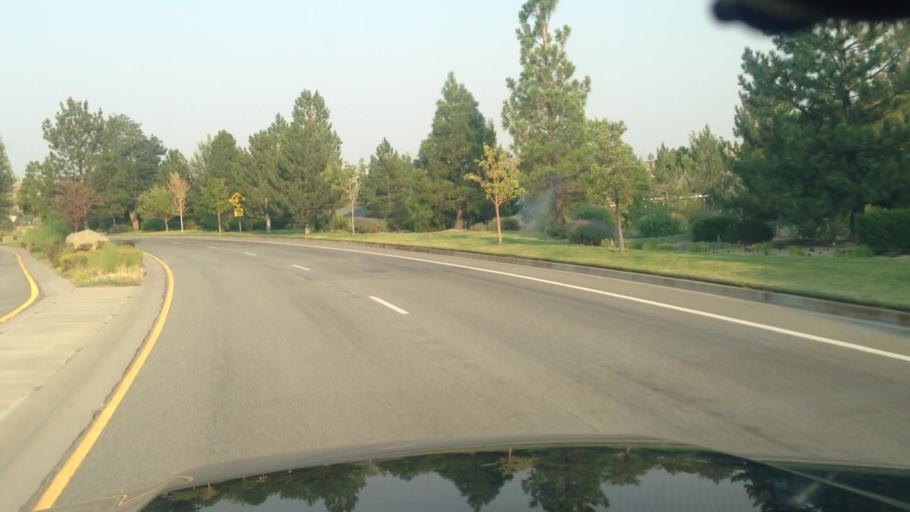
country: US
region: Nevada
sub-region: Washoe County
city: Mogul
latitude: 39.5325
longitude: -119.9182
